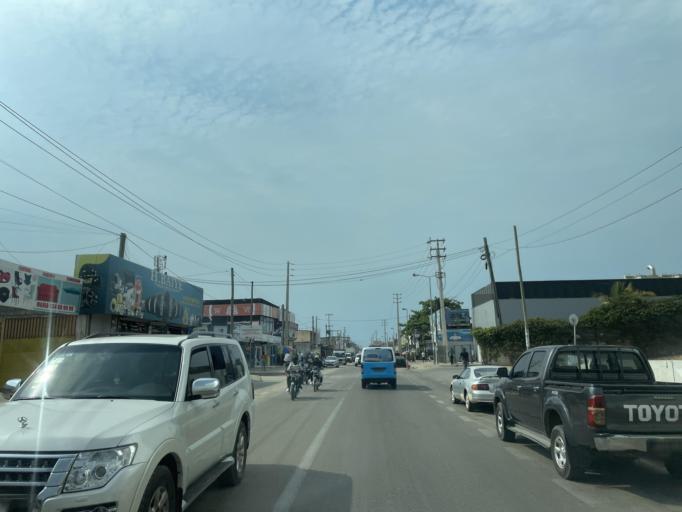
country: AO
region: Luanda
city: Luanda
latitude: -8.9029
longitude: 13.1884
